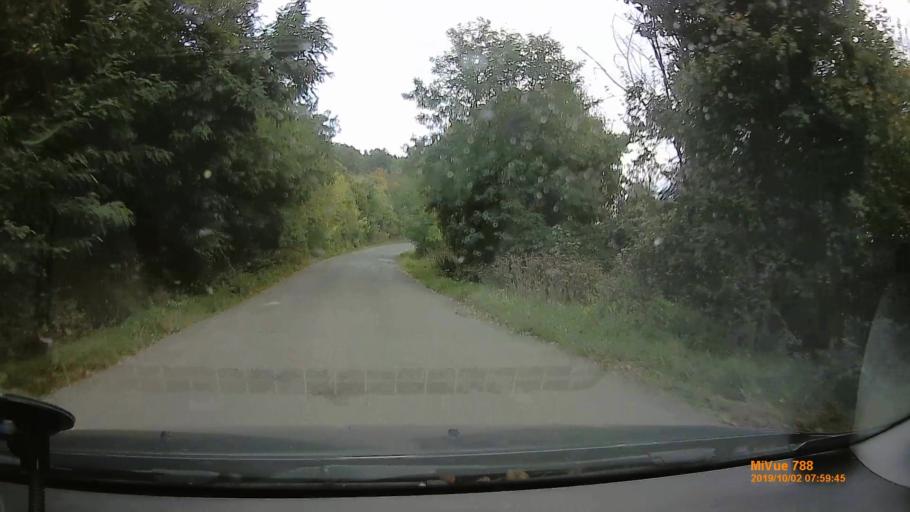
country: HU
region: Nograd
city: Tar
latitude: 47.9653
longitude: 19.7583
